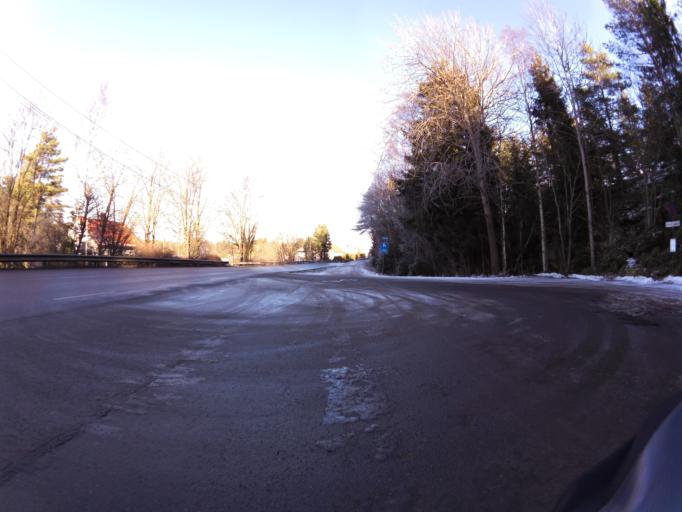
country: NO
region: Ostfold
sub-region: Fredrikstad
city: Fredrikstad
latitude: 59.2011
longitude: 10.8719
